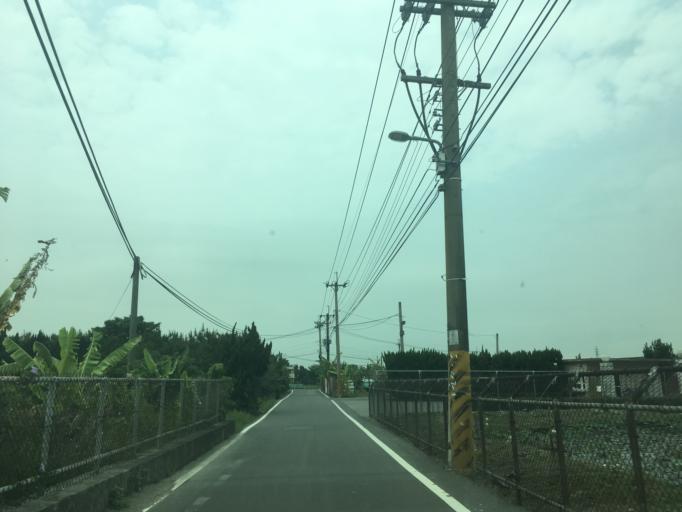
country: TW
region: Taiwan
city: Zhongxing New Village
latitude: 24.0393
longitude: 120.6837
